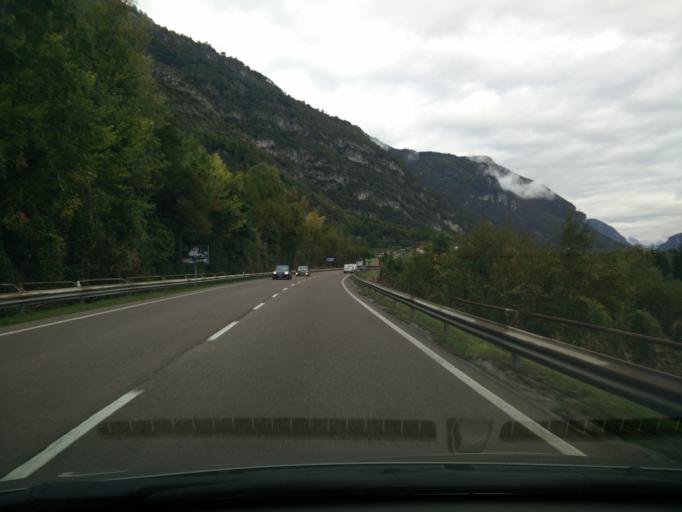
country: IT
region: Veneto
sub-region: Provincia di Belluno
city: Soverzene
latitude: 46.2193
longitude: 12.2865
